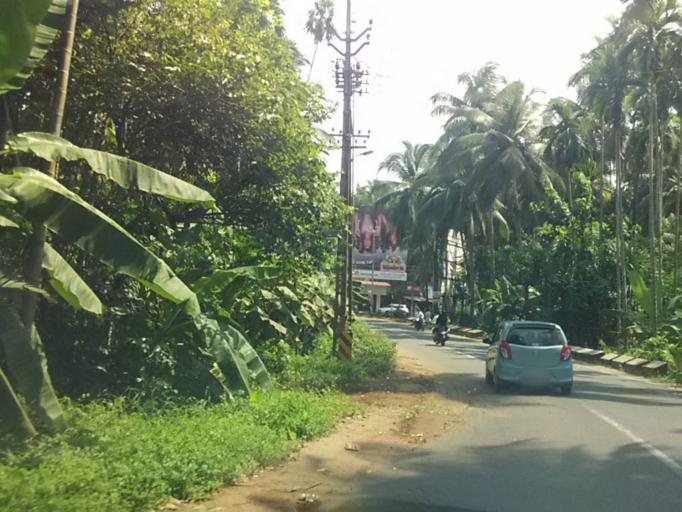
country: IN
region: Kerala
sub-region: Kozhikode
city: Kunnamangalam
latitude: 11.3304
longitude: 75.8911
